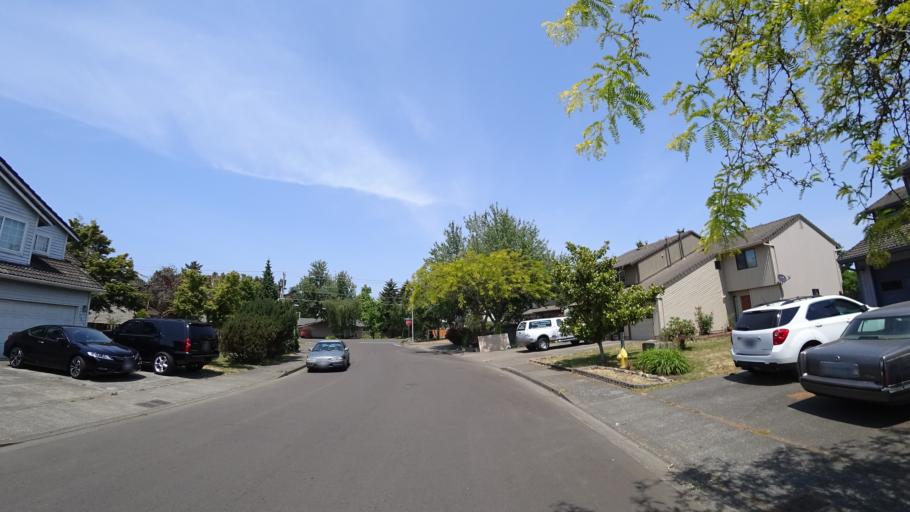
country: US
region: Oregon
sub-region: Washington County
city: Hillsboro
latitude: 45.4983
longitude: -122.9410
